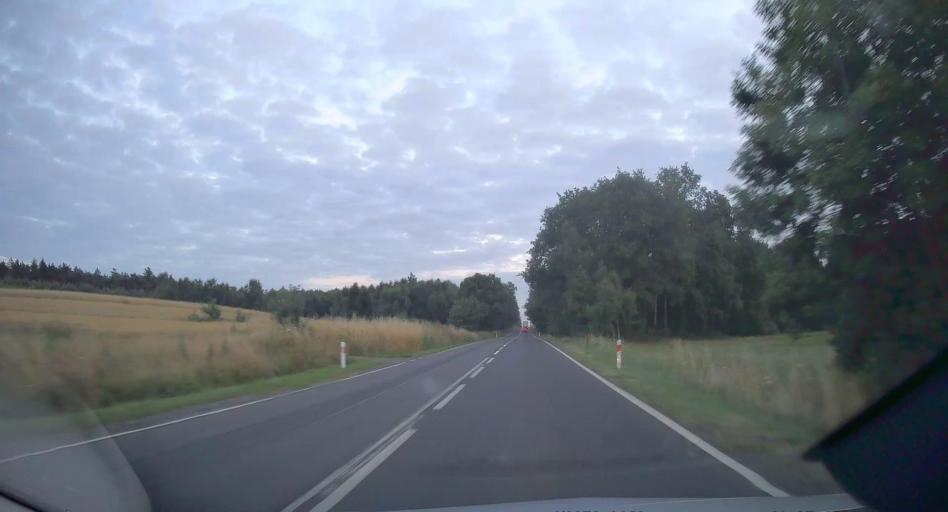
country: PL
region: Opole Voivodeship
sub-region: Powiat oleski
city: Dalachow
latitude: 51.1037
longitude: 18.6072
